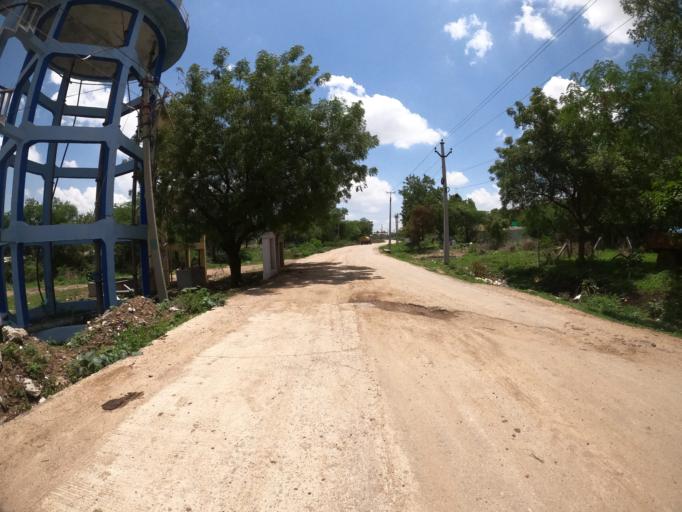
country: IN
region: Telangana
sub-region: Rangareddi
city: Singapur
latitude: 17.4424
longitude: 78.1575
